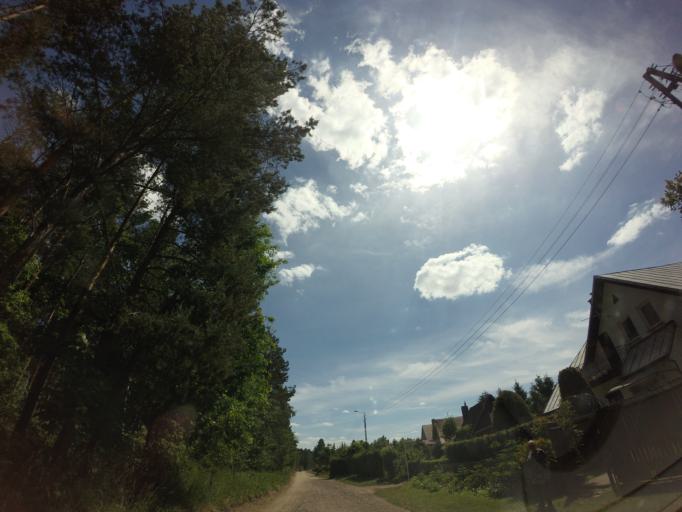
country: PL
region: West Pomeranian Voivodeship
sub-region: Powiat choszczenski
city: Drawno
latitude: 53.2113
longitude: 15.8351
